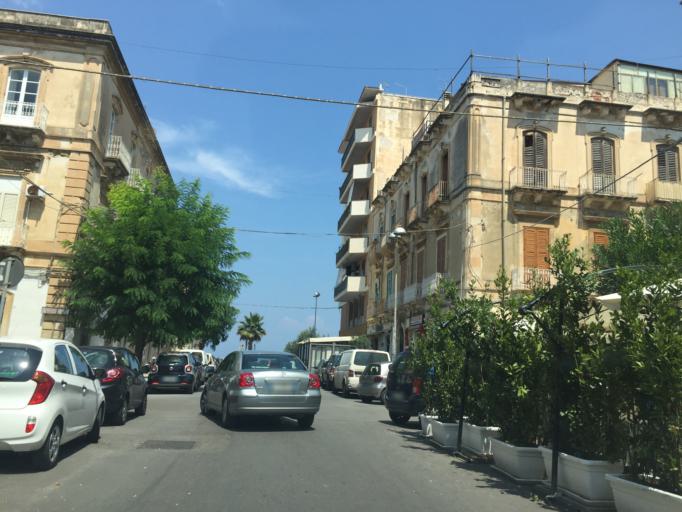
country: IT
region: Sicily
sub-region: Provincia di Siracusa
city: Siracusa
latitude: 37.0651
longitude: 15.2930
